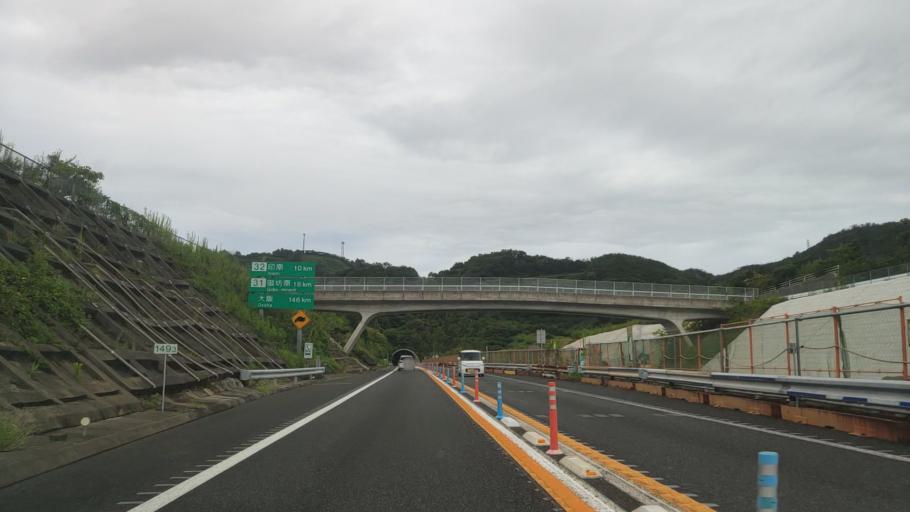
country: JP
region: Wakayama
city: Tanabe
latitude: 33.7840
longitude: 135.3144
